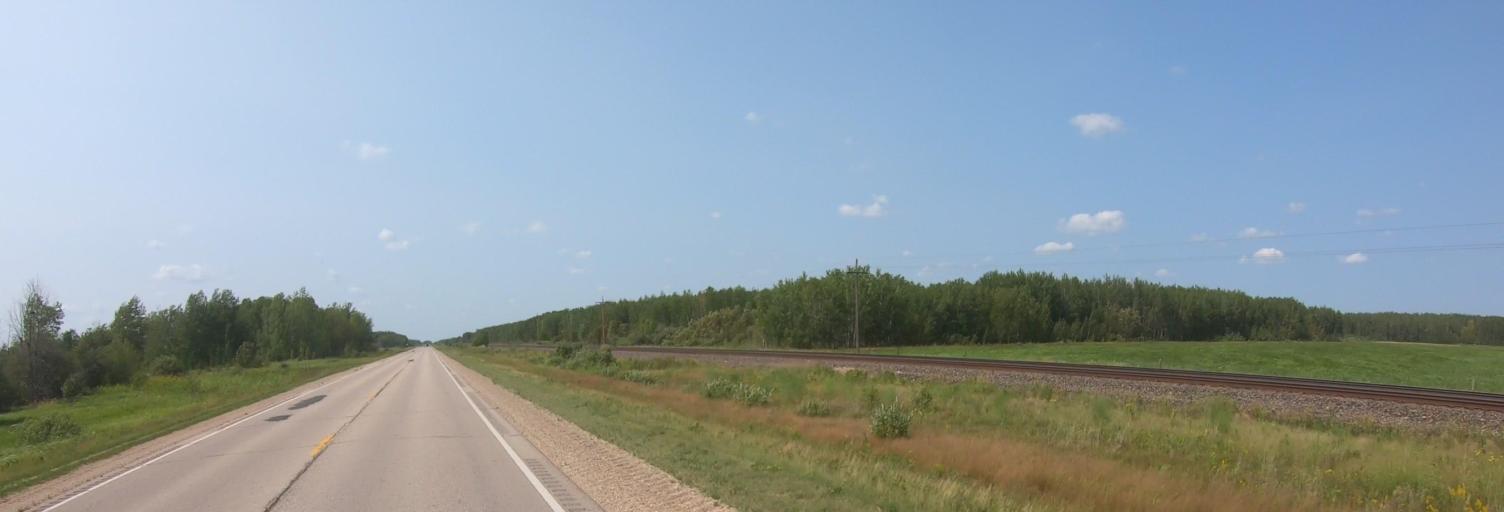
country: US
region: Minnesota
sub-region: Lake of the Woods County
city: Baudette
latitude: 48.7286
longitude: -94.7876
